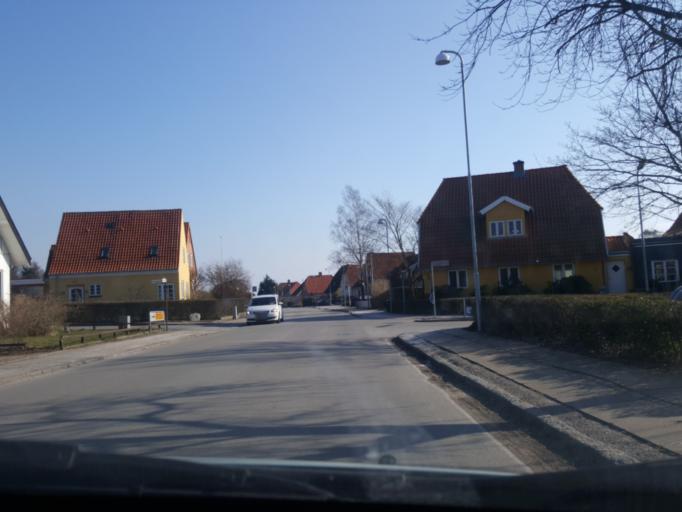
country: DK
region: Zealand
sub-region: Kalundborg Kommune
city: Kalundborg
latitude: 55.6824
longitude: 11.0692
